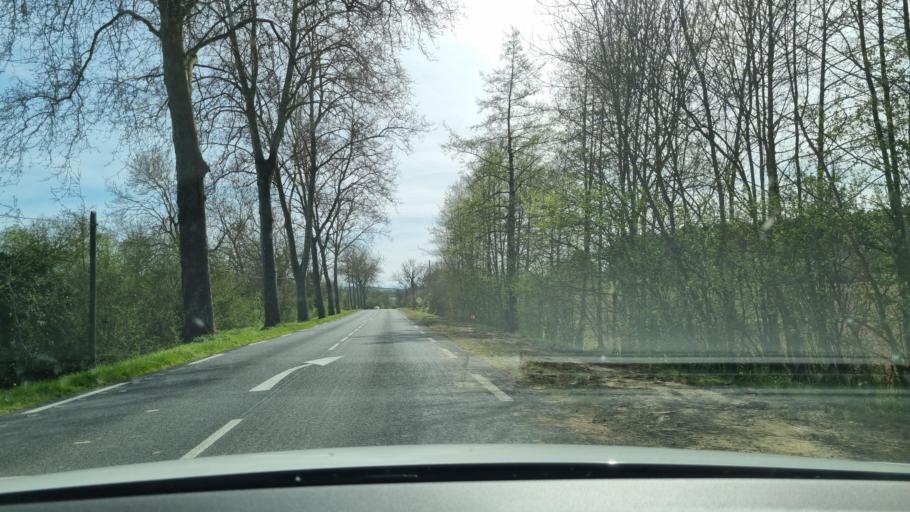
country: FR
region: Midi-Pyrenees
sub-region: Departement du Gers
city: Lombez
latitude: 43.4043
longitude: 0.7983
